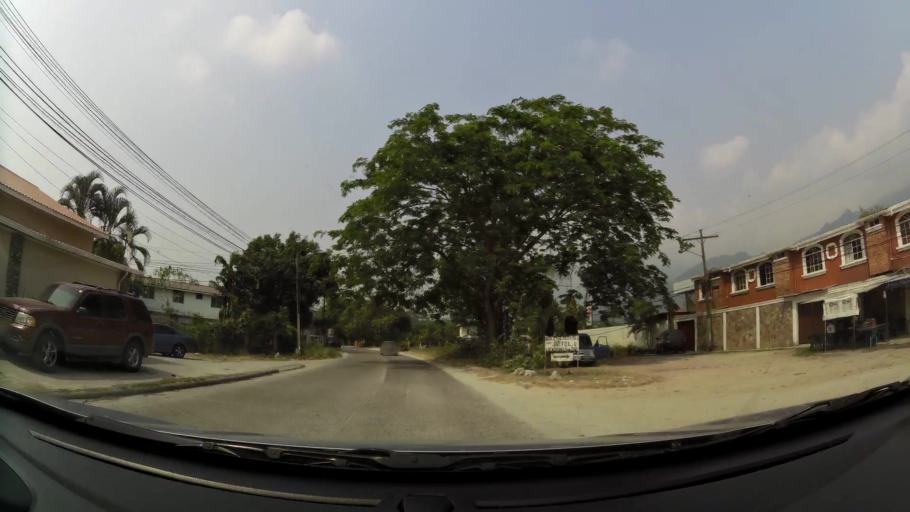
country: HN
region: Cortes
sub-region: San Pedro Sula
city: Pena Blanca
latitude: 15.5474
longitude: -88.0278
